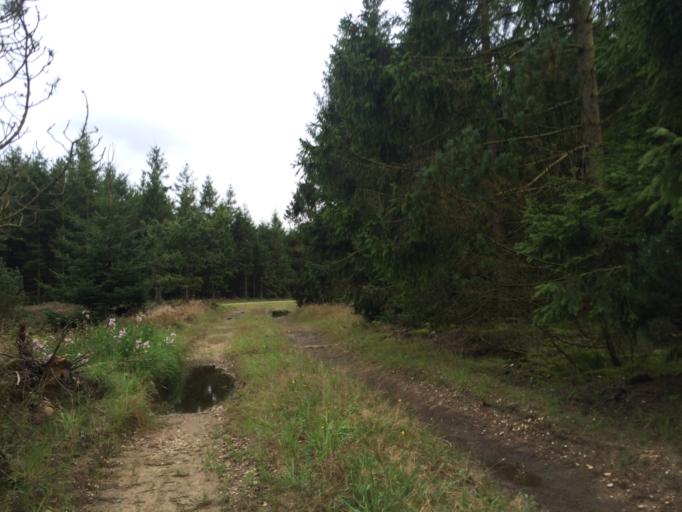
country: DK
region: Central Jutland
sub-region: Holstebro Kommune
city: Ulfborg
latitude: 56.2177
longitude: 8.3946
